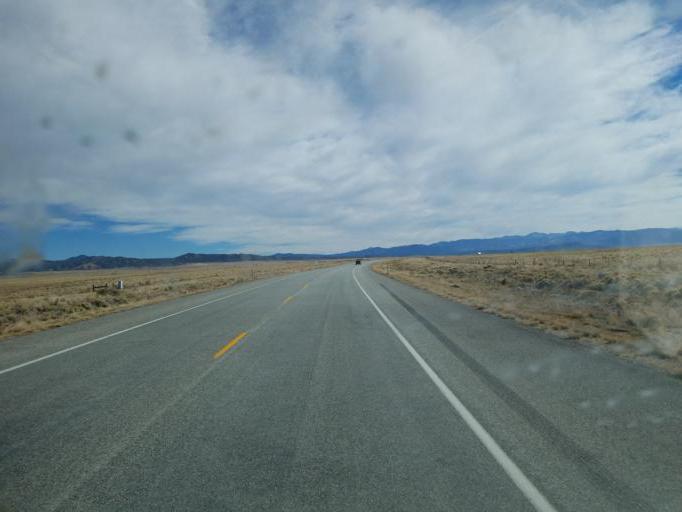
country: US
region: Colorado
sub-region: Alamosa County
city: Alamosa East
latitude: 37.4749
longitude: -105.5880
